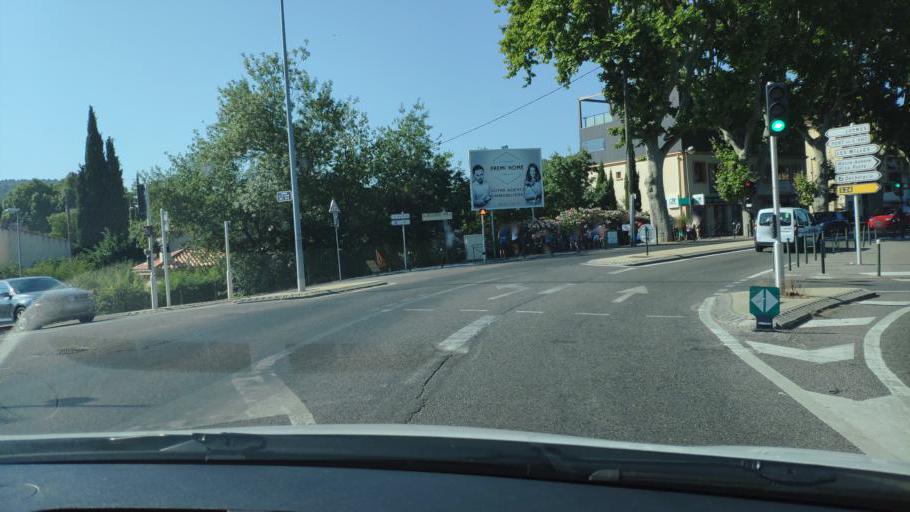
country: FR
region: Provence-Alpes-Cote d'Azur
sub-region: Departement des Bouches-du-Rhone
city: Aix-en-Provence
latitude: 43.5106
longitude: 5.4422
